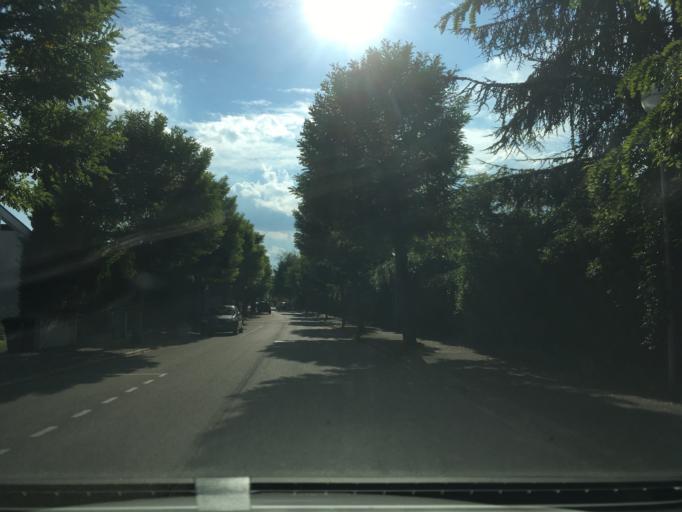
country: FR
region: Alsace
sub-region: Departement du Haut-Rhin
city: Colmar
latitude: 48.0624
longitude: 7.3425
